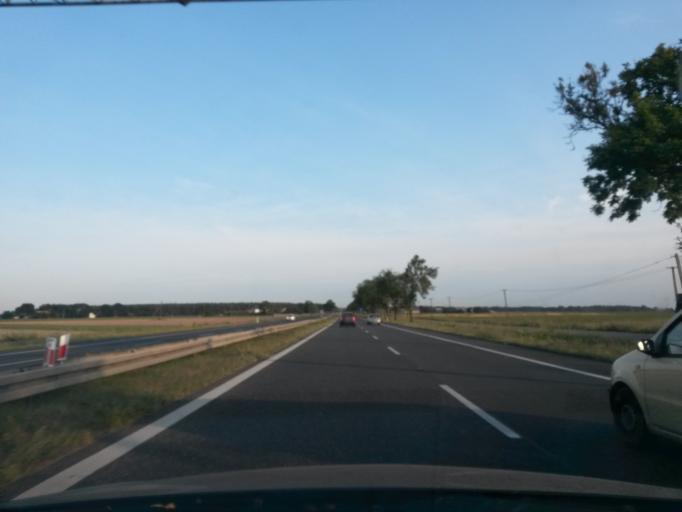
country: PL
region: Masovian Voivodeship
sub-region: Powiat nowodworski
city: Zakroczym
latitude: 52.4688
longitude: 20.5698
